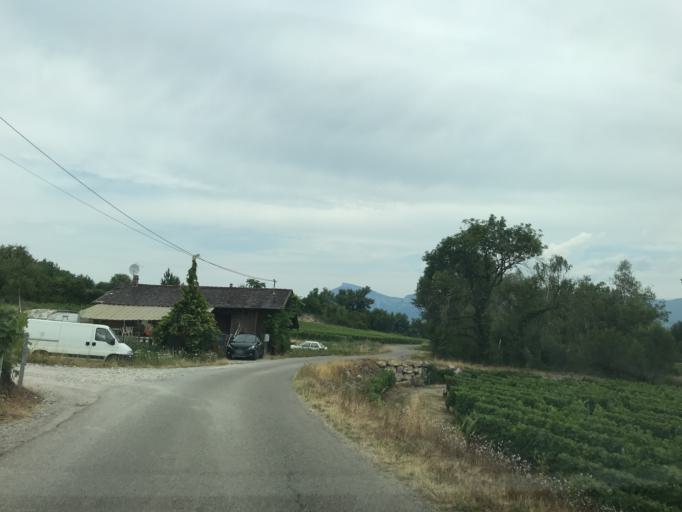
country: FR
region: Rhone-Alpes
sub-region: Departement de l'Isere
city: Chapareillan
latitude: 45.4886
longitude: 5.9656
